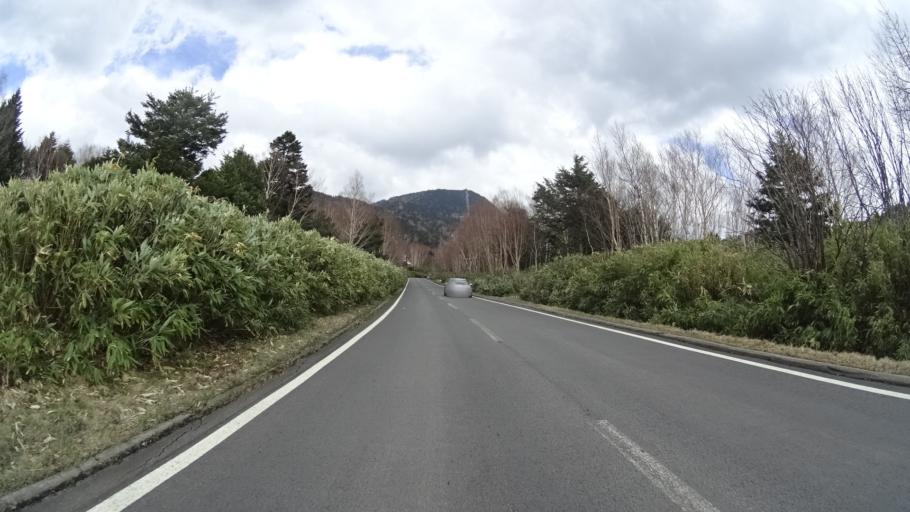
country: JP
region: Nagano
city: Nakano
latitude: 36.6796
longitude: 138.5053
